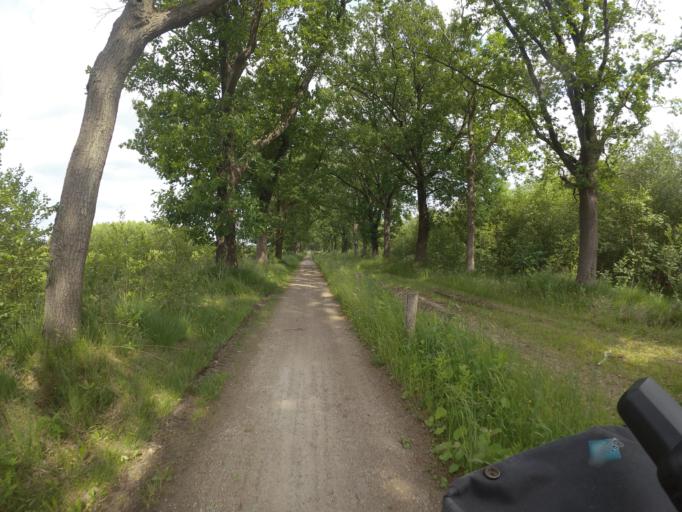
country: NL
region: Drenthe
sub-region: Gemeente Assen
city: Assen
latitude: 53.0040
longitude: 6.4451
